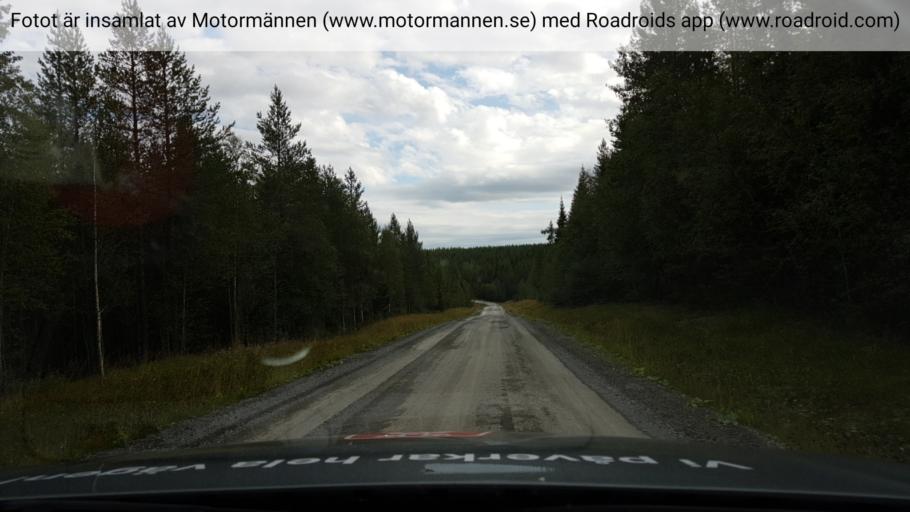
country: SE
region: Jaemtland
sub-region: Krokoms Kommun
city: Valla
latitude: 63.6741
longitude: 13.6960
